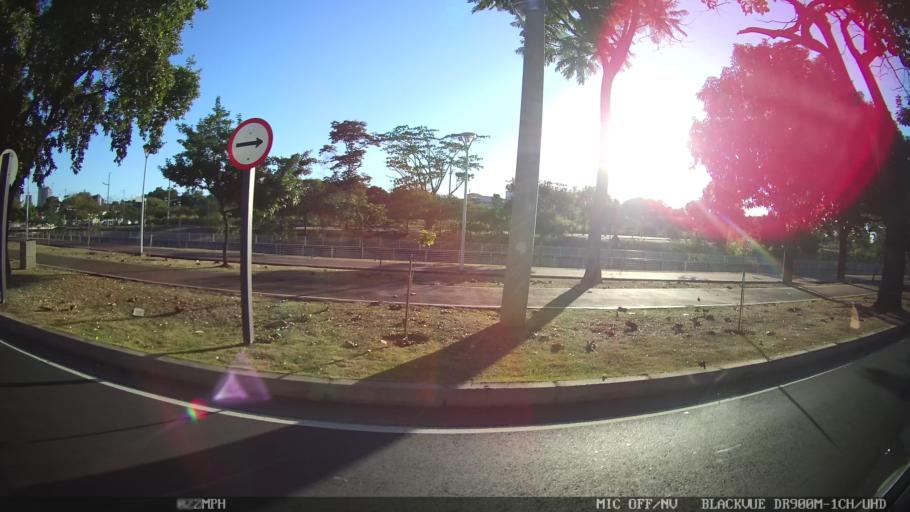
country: BR
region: Sao Paulo
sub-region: Sao Jose Do Rio Preto
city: Sao Jose do Rio Preto
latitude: -20.7949
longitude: -49.3761
